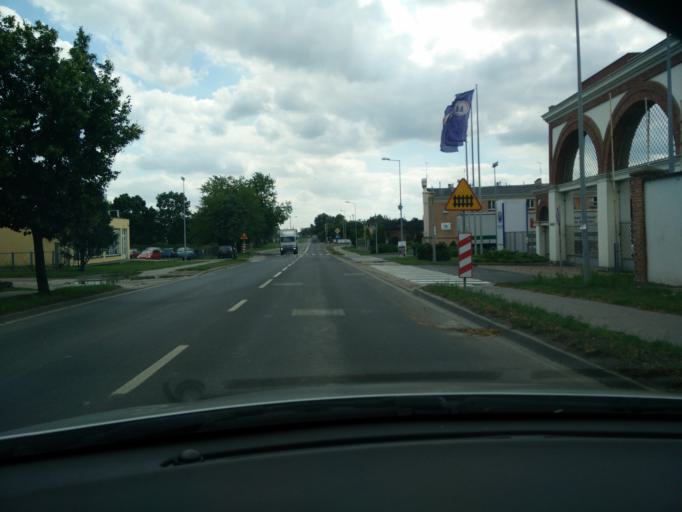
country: PL
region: Greater Poland Voivodeship
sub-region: Powiat sredzki
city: Sroda Wielkopolska
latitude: 52.2179
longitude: 17.2791
